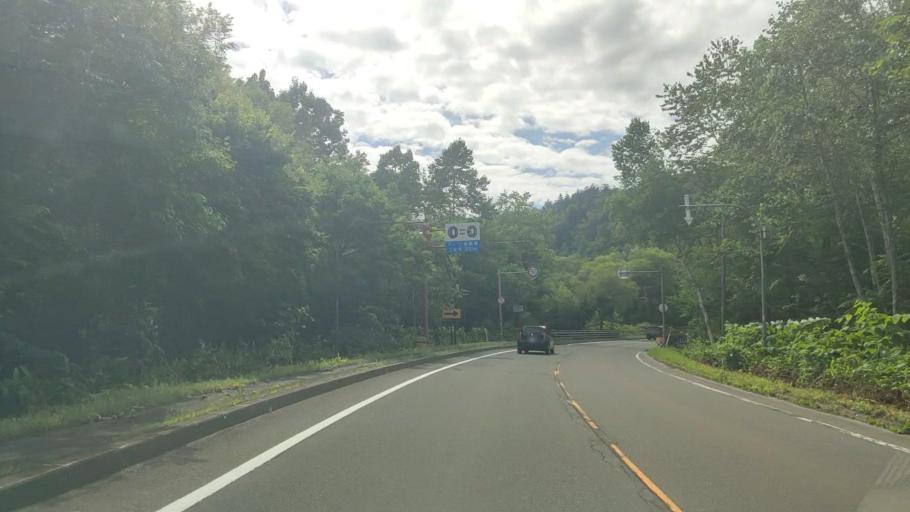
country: JP
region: Hokkaido
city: Shiraoi
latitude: 42.7165
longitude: 141.2197
